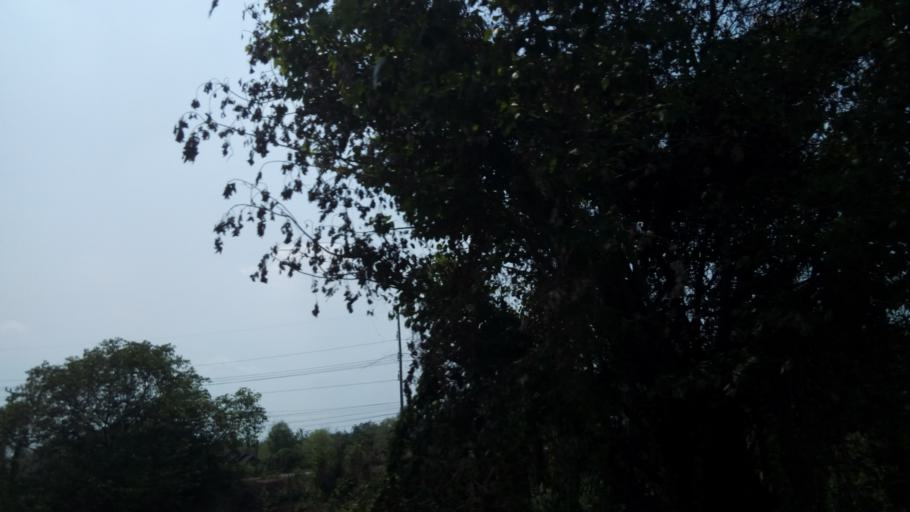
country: TH
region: Sara Buri
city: Nong Khae
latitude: 14.3262
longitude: 100.8710
